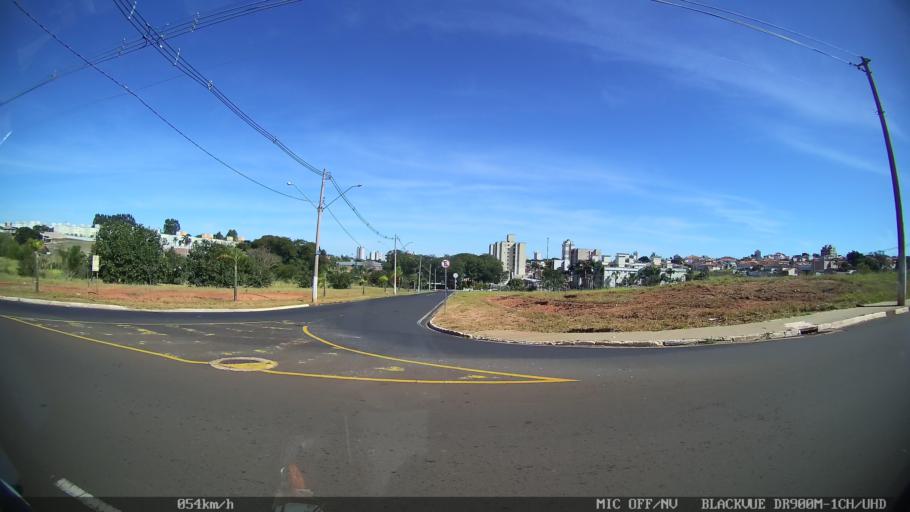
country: BR
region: Sao Paulo
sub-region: Franca
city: Franca
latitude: -20.5353
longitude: -47.3760
